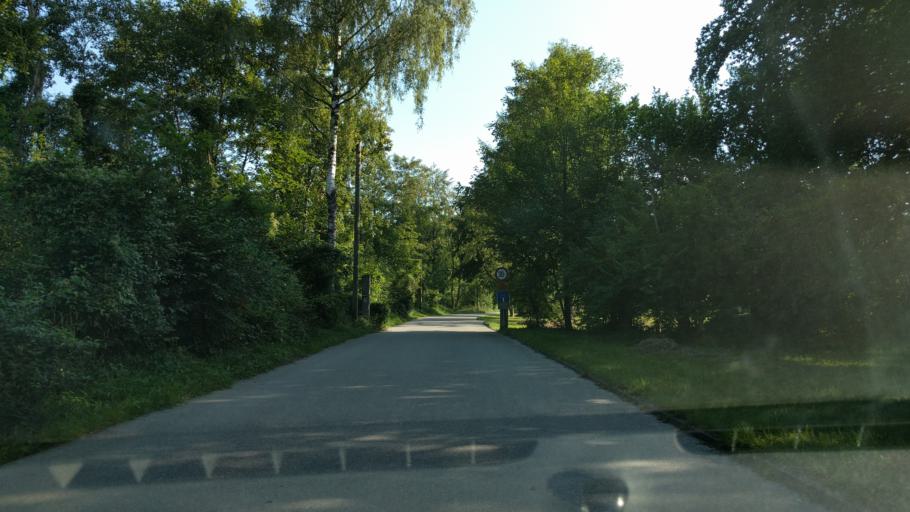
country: DE
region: Bavaria
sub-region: Upper Bavaria
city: Grunwald
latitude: 48.0331
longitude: 11.5075
